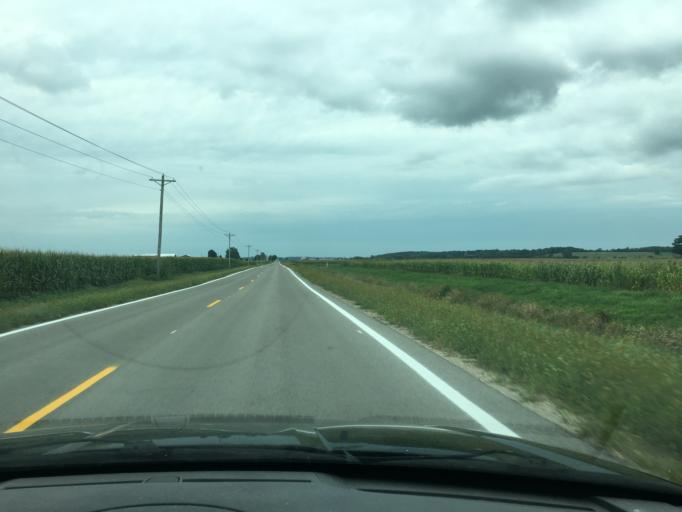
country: US
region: Ohio
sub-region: Champaign County
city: Urbana
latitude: 40.1596
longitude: -83.7844
